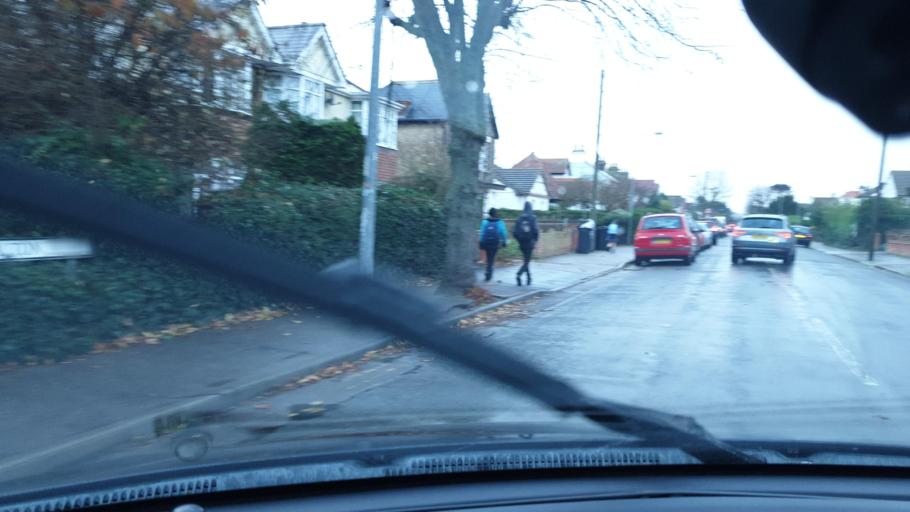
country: GB
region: England
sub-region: Essex
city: Clacton-on-Sea
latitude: 51.7950
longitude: 1.1592
